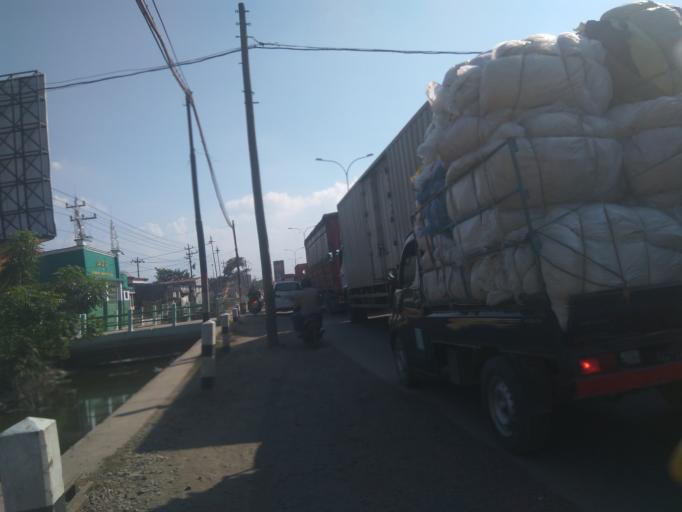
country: ID
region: Central Java
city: Semarang
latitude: -6.9540
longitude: 110.4743
